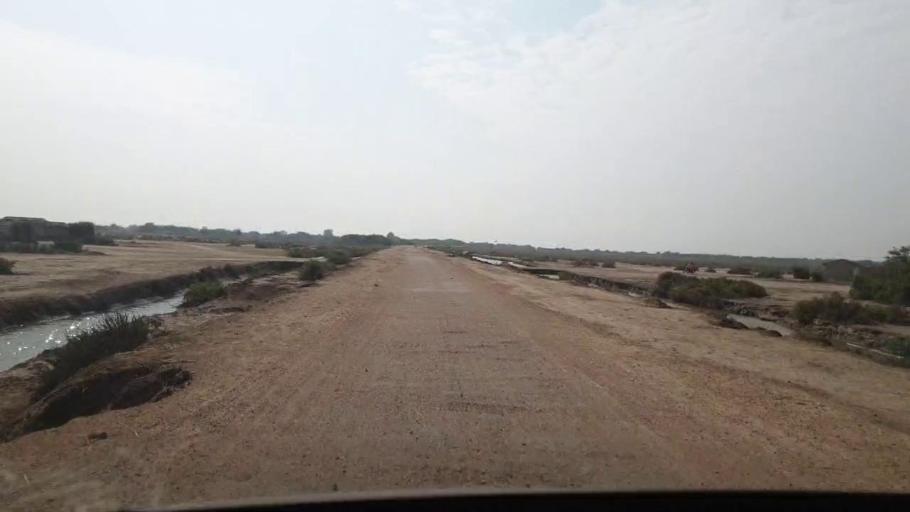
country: PK
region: Sindh
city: Chuhar Jamali
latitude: 24.2432
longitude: 67.9895
